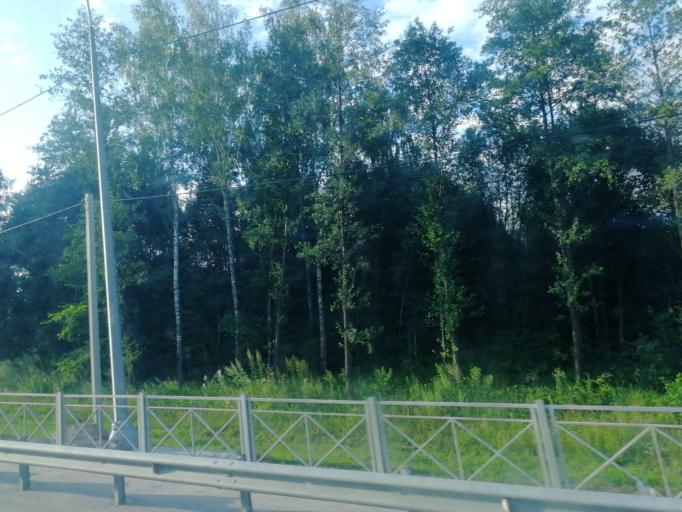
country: RU
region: Kaluga
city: Kaluga
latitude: 54.4371
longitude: 36.3415
